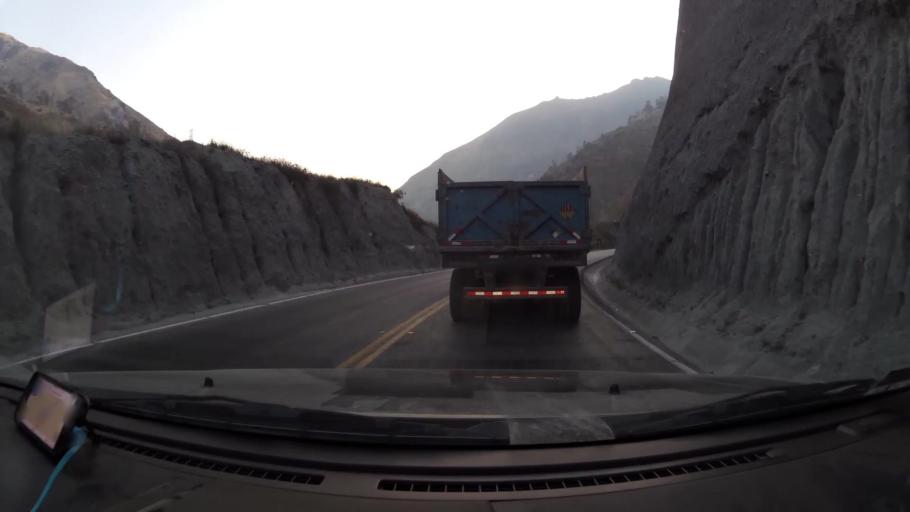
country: PE
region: Lima
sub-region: Provincia de Huarochiri
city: Matucana
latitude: -11.8542
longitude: -76.4043
